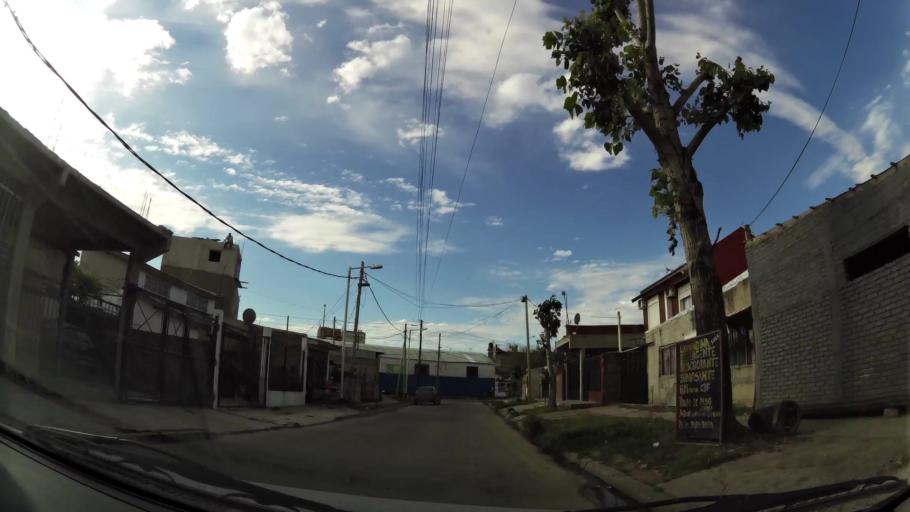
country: AR
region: Buenos Aires
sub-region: Partido de Lanus
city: Lanus
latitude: -34.7042
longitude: -58.3583
